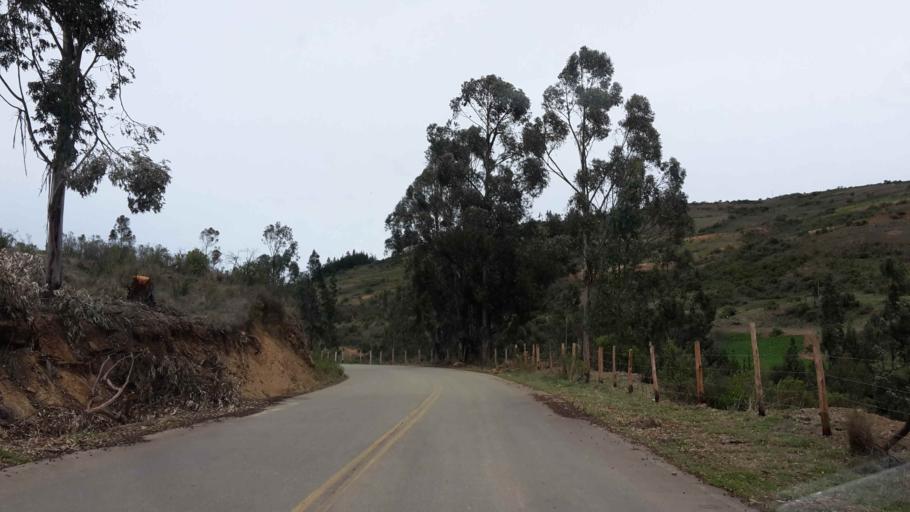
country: BO
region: Cochabamba
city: Totora
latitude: -17.7125
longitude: -65.2092
